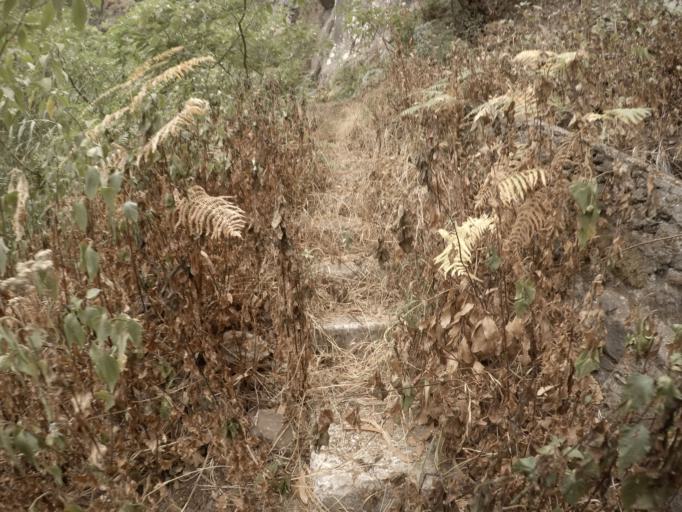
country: PT
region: Madeira
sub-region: Camara de Lobos
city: Curral das Freiras
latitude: 32.6860
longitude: -16.9644
